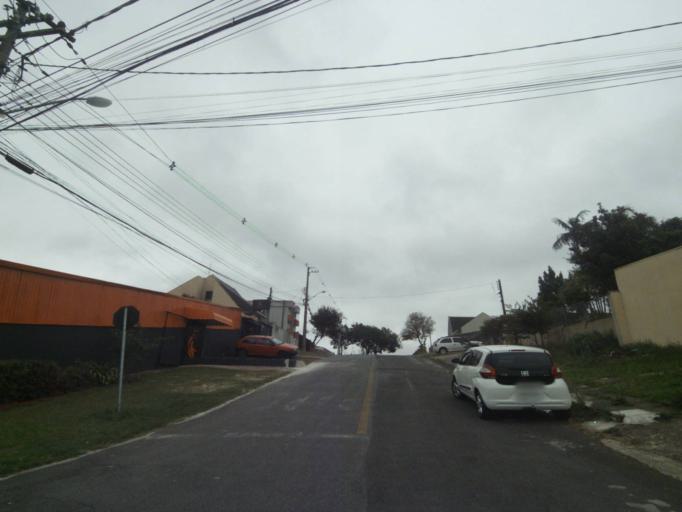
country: BR
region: Parana
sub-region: Curitiba
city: Curitiba
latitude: -25.4662
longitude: -49.2748
